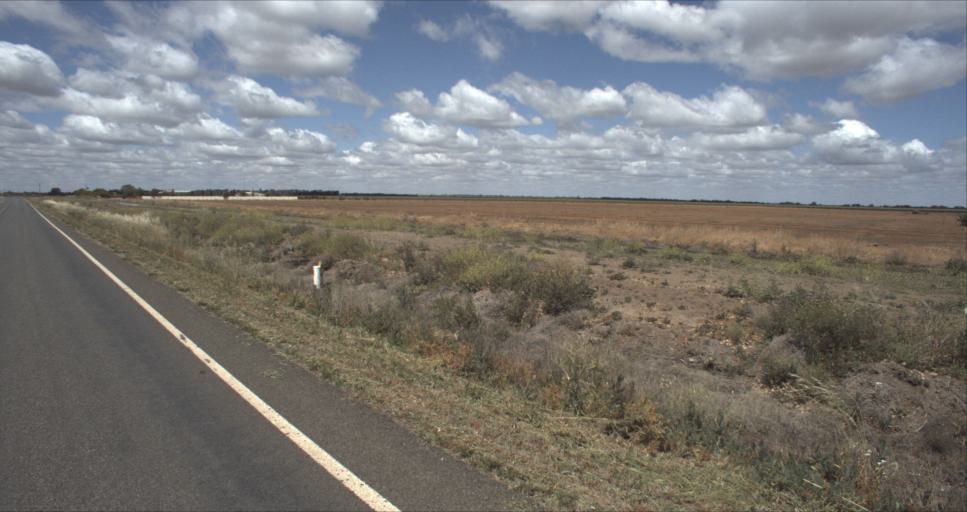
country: AU
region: New South Wales
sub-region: Murrumbidgee Shire
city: Darlington Point
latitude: -34.4837
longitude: 146.1573
